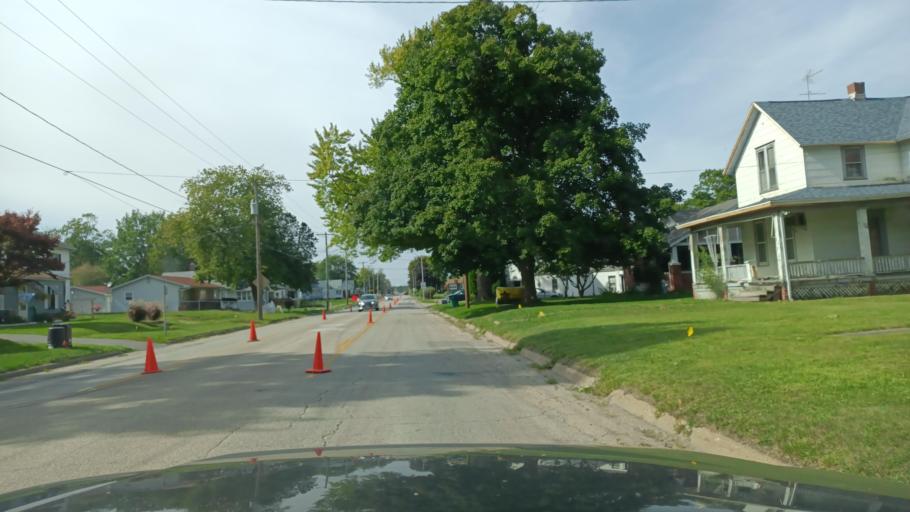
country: US
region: Illinois
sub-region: Knox County
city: Galesburg
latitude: 40.9421
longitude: -90.3470
